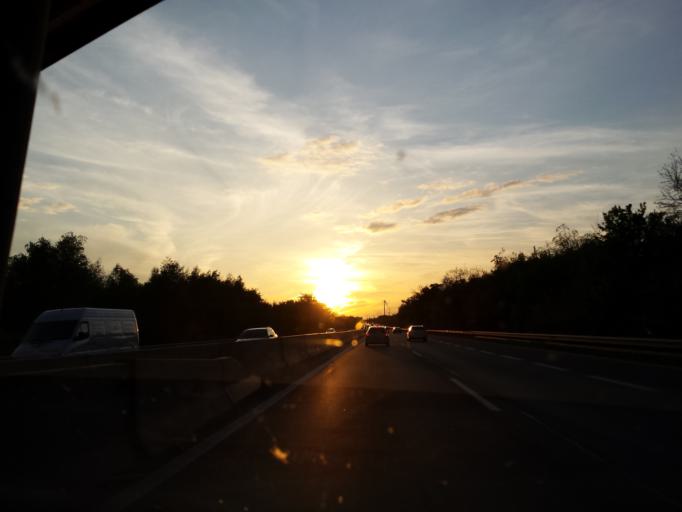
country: AT
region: Burgenland
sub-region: Politischer Bezirk Neusiedl am See
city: Bruckneudorf
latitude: 48.0360
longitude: 16.8134
